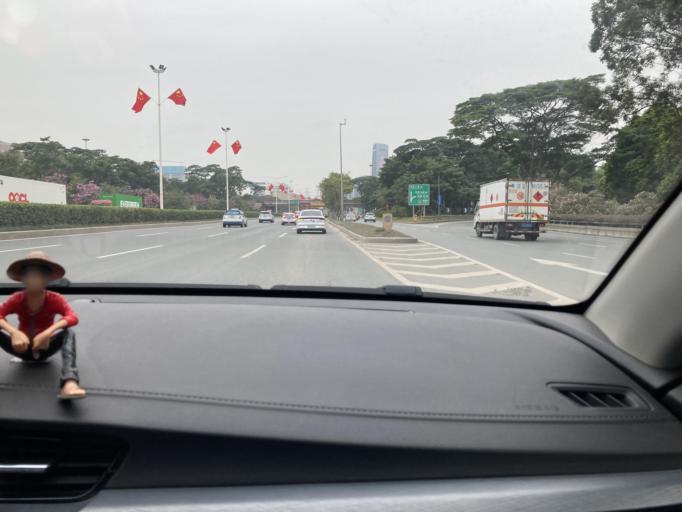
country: CN
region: Guangdong
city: Nanshan
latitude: 22.5554
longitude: 113.9315
